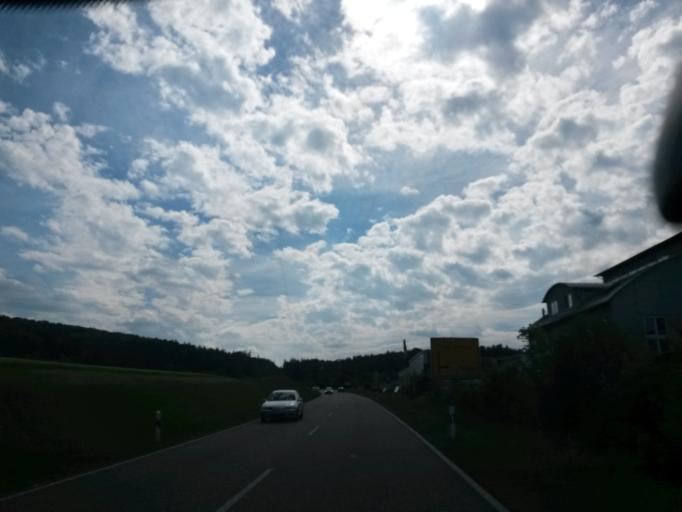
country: DE
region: Baden-Wuerttemberg
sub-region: Karlsruhe Region
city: Simmozheim
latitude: 48.7455
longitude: 8.8101
